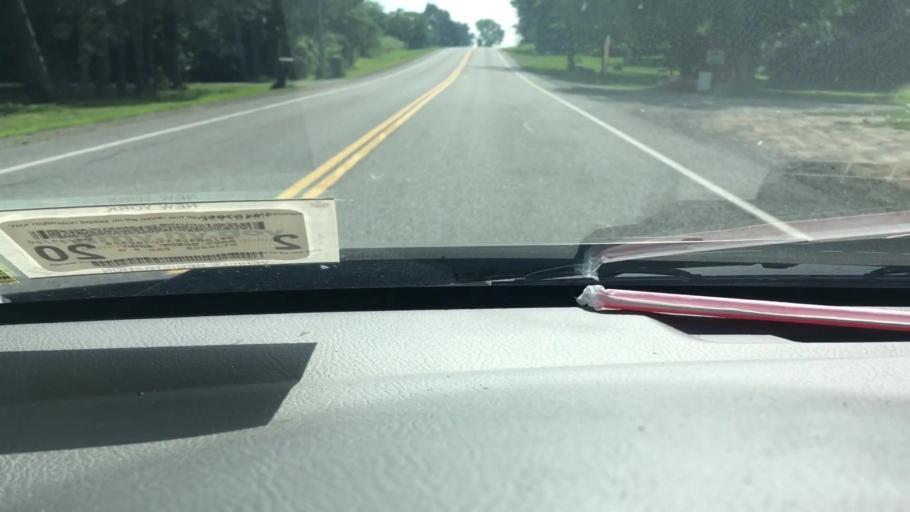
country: US
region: New York
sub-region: Genesee County
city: Batavia
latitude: 43.0398
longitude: -78.1439
